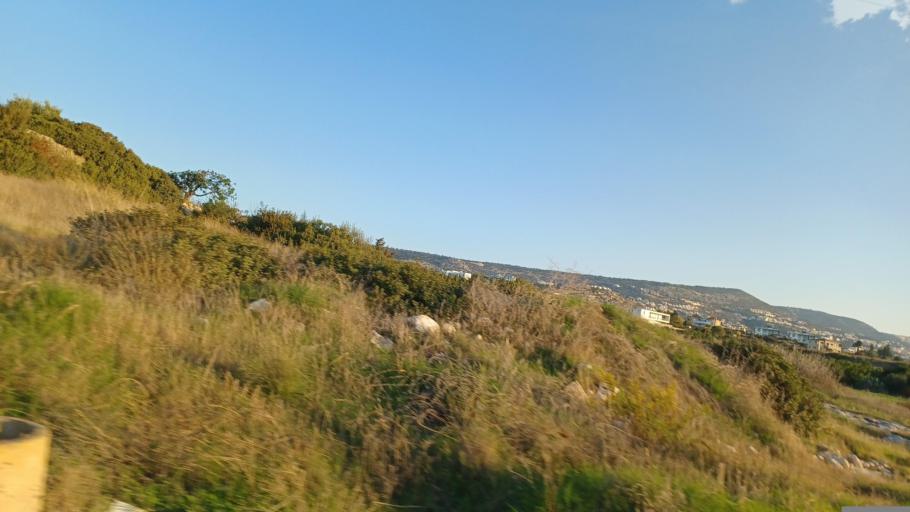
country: CY
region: Pafos
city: Pegeia
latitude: 34.8682
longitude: 32.3559
